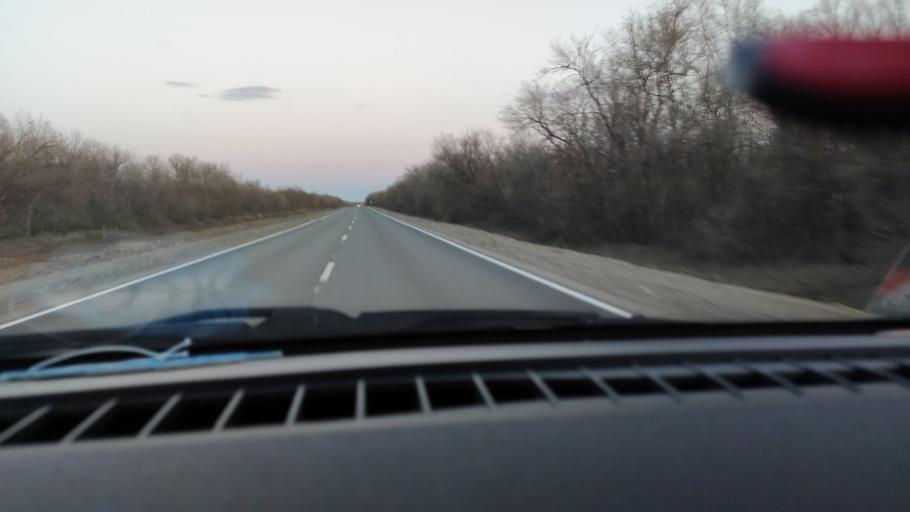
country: RU
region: Saratov
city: Privolzhskiy
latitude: 51.1666
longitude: 45.9455
